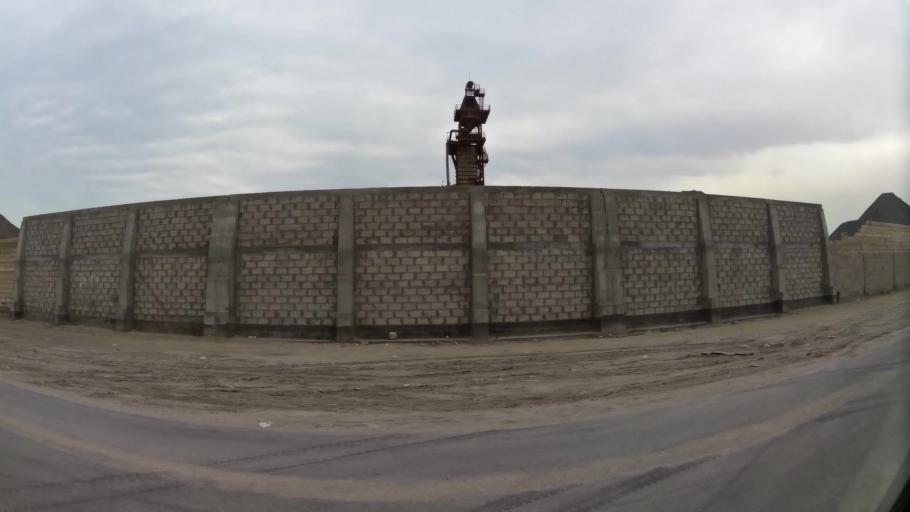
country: BH
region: Northern
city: Sitrah
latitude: 26.1298
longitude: 50.6059
